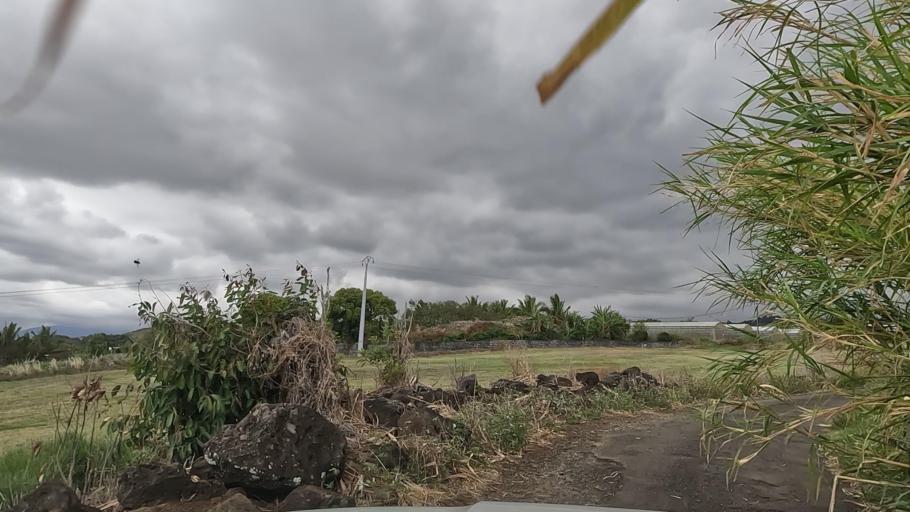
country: RE
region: Reunion
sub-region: Reunion
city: Saint-Pierre
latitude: -21.3418
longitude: 55.5193
